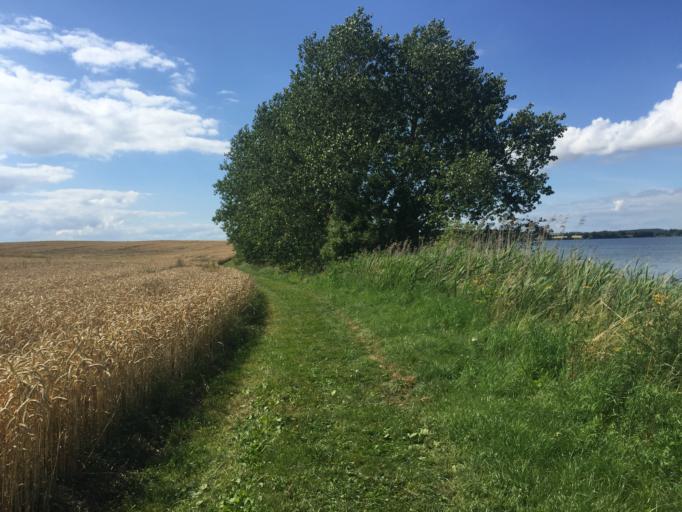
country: DK
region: South Denmark
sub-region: Faaborg-Midtfyn Kommune
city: Faaborg
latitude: 55.0689
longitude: 10.2458
